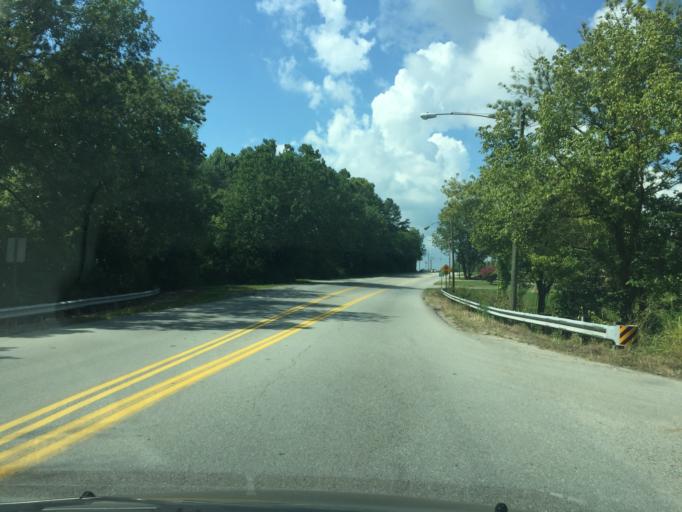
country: US
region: Tennessee
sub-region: Hamilton County
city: East Chattanooga
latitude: 35.0531
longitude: -85.2111
